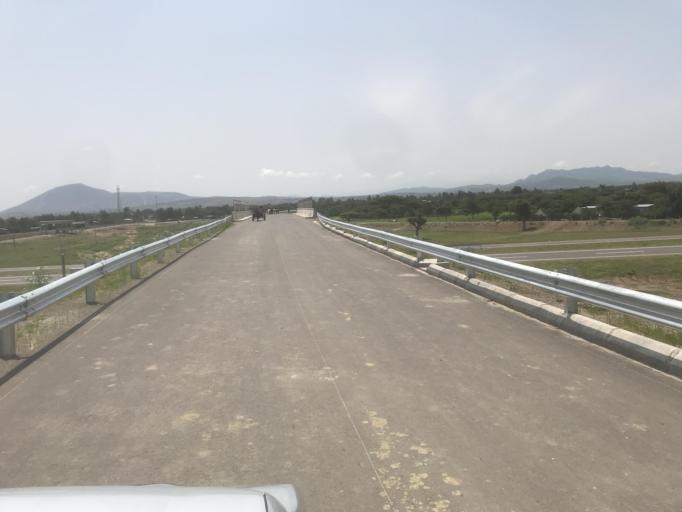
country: ET
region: Oromiya
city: Mojo
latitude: 8.3025
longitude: 38.9355
